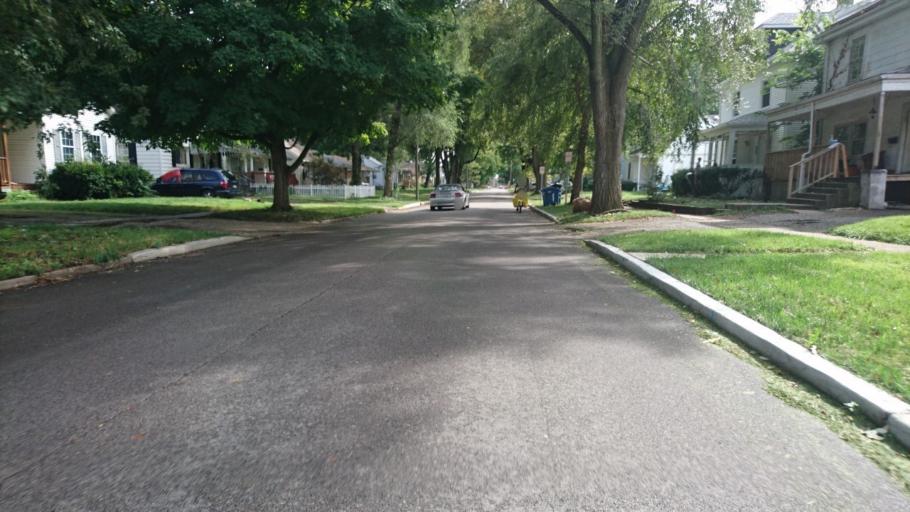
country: US
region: Illinois
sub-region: Sangamon County
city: Springfield
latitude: 39.7823
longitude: -89.6545
